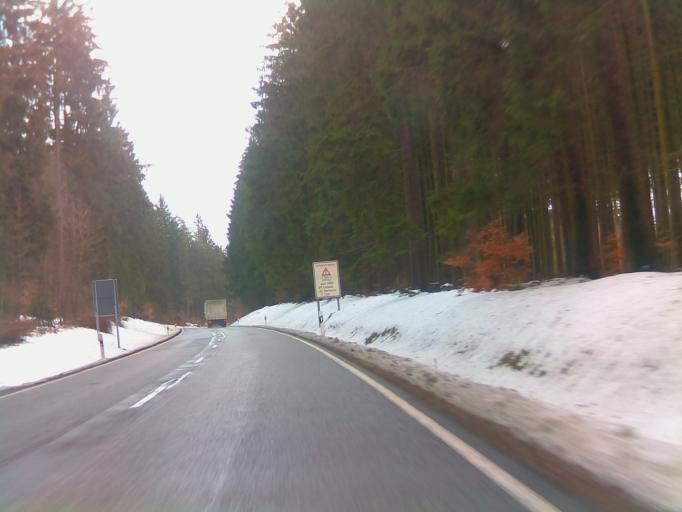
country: DE
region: Baden-Wuerttemberg
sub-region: Karlsruhe Region
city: Fahrenbach
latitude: 49.4640
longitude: 9.1206
